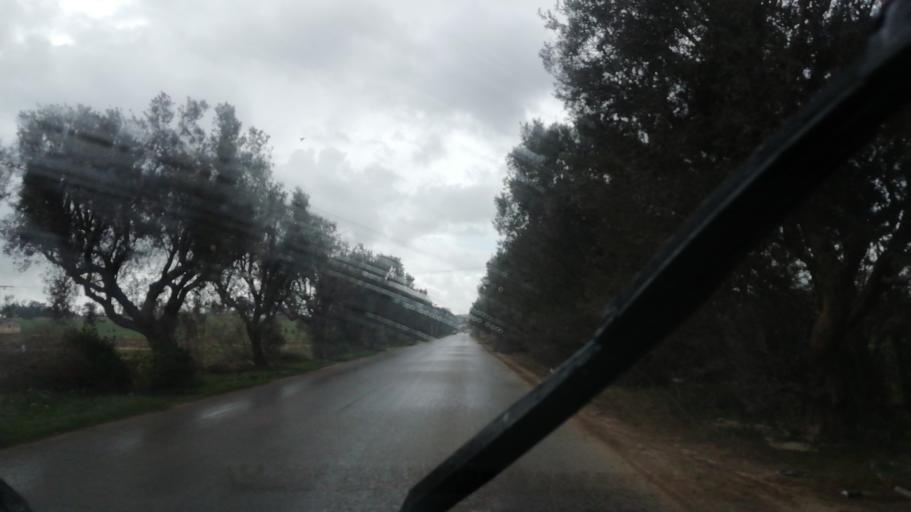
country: DZ
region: Oran
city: Sidi ech Chahmi
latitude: 35.6379
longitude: -0.5256
